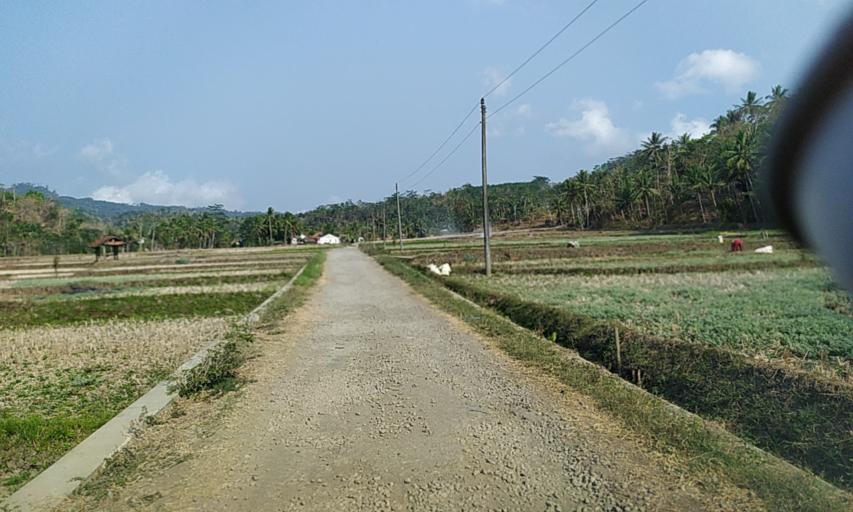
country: ID
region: Central Java
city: Jambuluwuk
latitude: -7.3148
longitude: 108.8752
